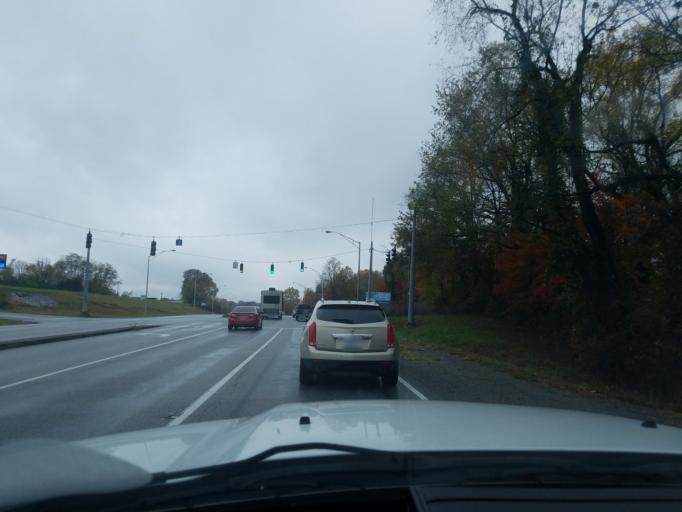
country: US
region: Kentucky
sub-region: Taylor County
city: Campbellsville
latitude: 37.3395
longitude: -85.3551
